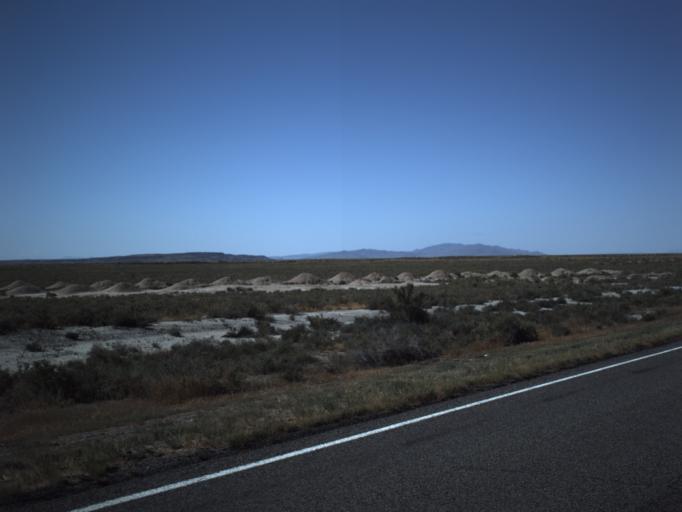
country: US
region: Utah
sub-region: Millard County
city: Delta
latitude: 39.3246
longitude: -112.7327
